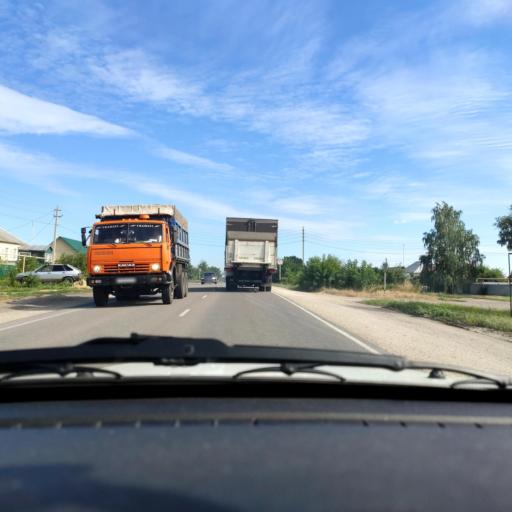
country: RU
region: Voronezj
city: Orlovo
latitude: 51.7544
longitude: 39.5880
